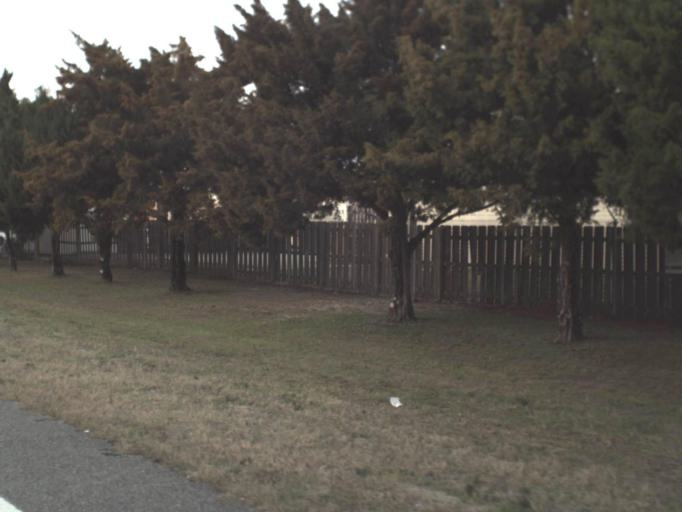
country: US
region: Florida
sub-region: Bay County
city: Tyndall Air Force Base
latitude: 30.0670
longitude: -85.5864
